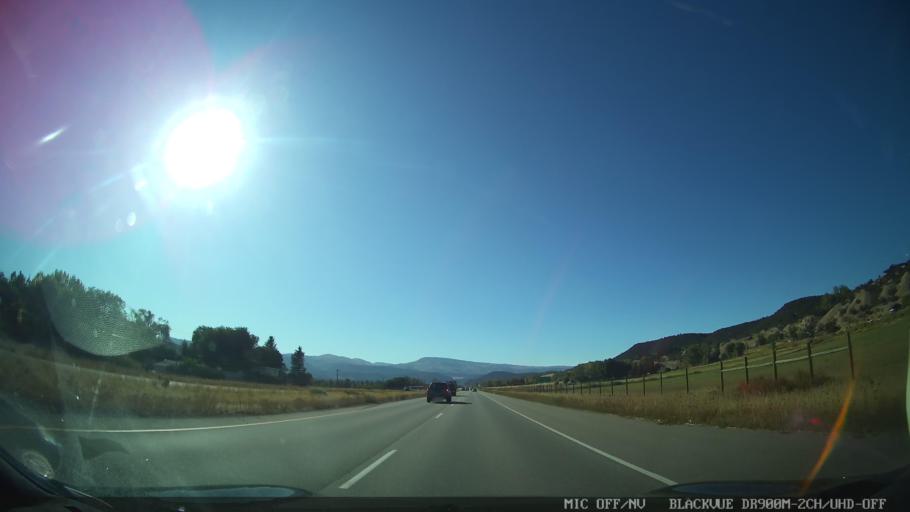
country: US
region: Colorado
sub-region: Eagle County
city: El Jebel
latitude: 39.4076
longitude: -107.1465
